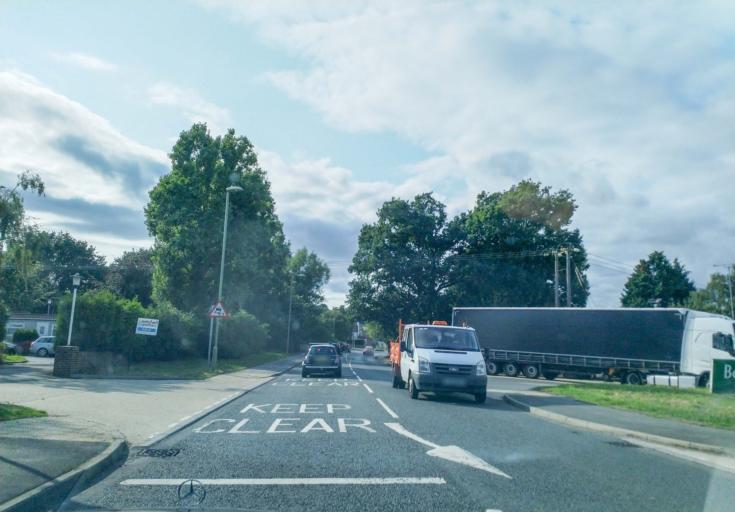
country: GB
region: England
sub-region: Surrey
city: Frimley
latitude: 51.3153
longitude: -0.7632
